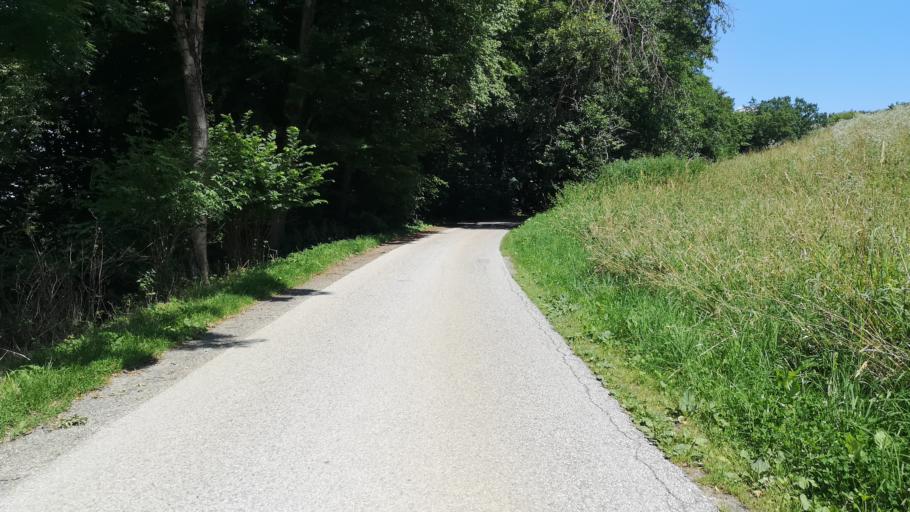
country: AT
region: Styria
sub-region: Politischer Bezirk Graz-Umgebung
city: Werndorf
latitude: 46.9171
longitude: 15.4989
